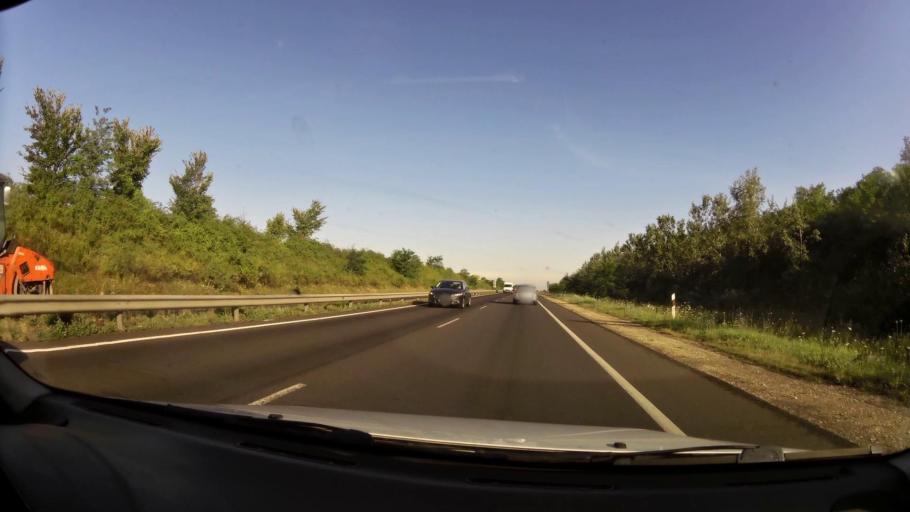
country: HU
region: Pest
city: Cegledbercel
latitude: 47.2247
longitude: 19.6866
